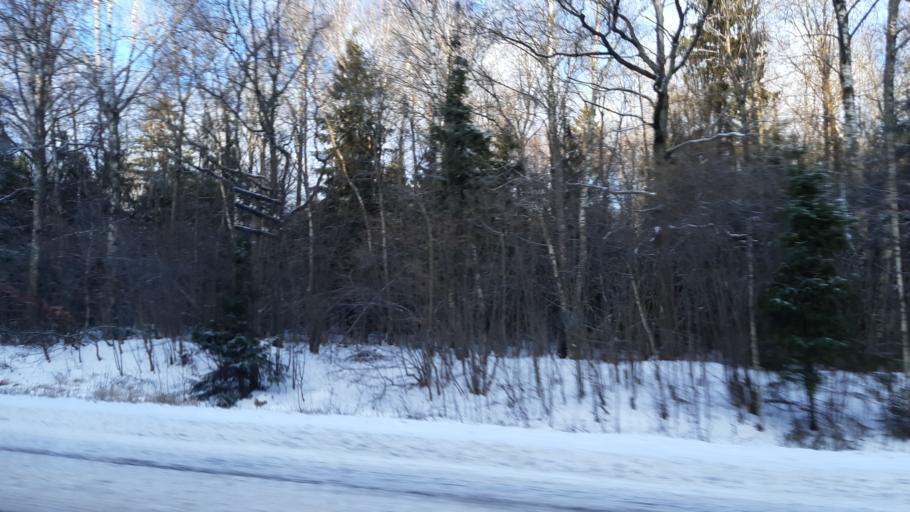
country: RU
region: Moskovskaya
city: Svatkovo
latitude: 56.3045
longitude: 38.3366
